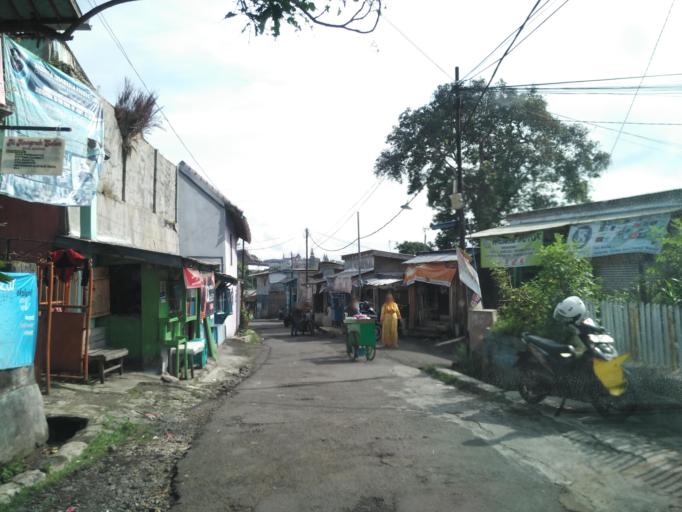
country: ID
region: West Java
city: Sukabumi
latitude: -6.7483
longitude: 107.0483
